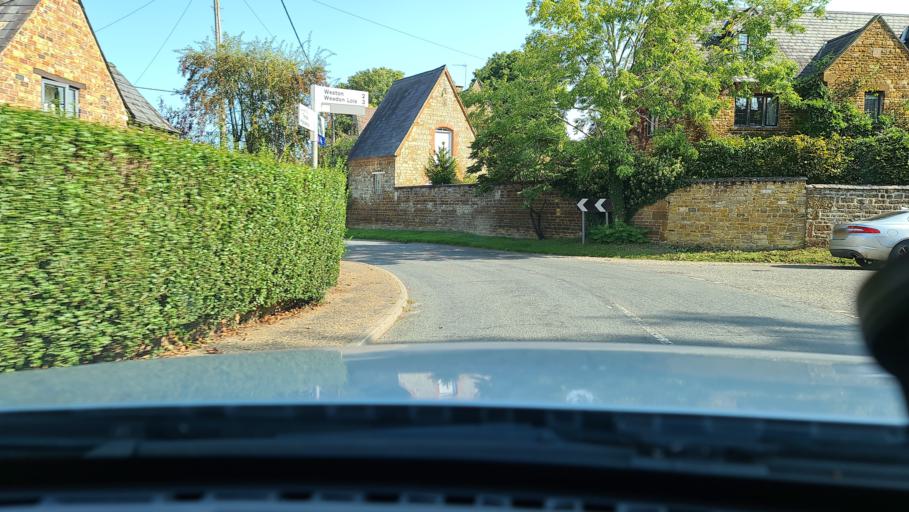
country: GB
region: England
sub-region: Northamptonshire
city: Brackley
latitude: 52.1378
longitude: -1.1623
